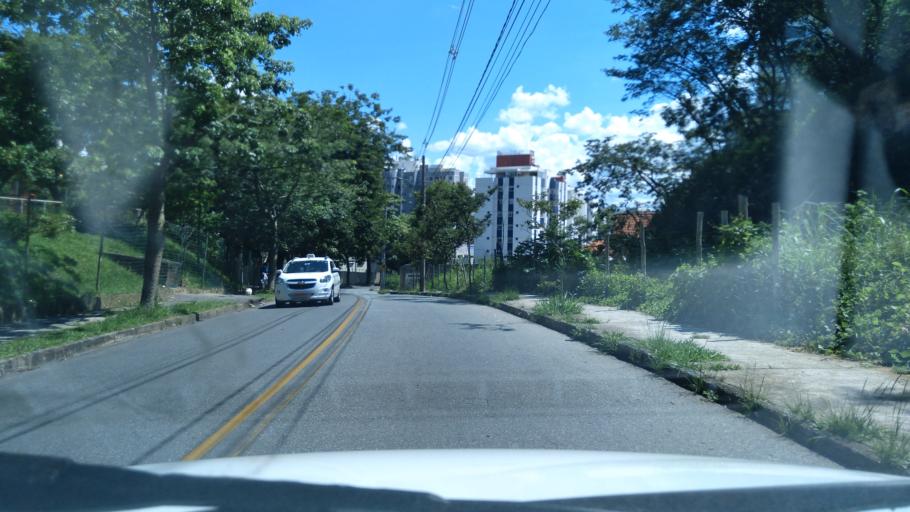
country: BR
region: Minas Gerais
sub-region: Belo Horizonte
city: Belo Horizonte
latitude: -19.8729
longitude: -43.9145
